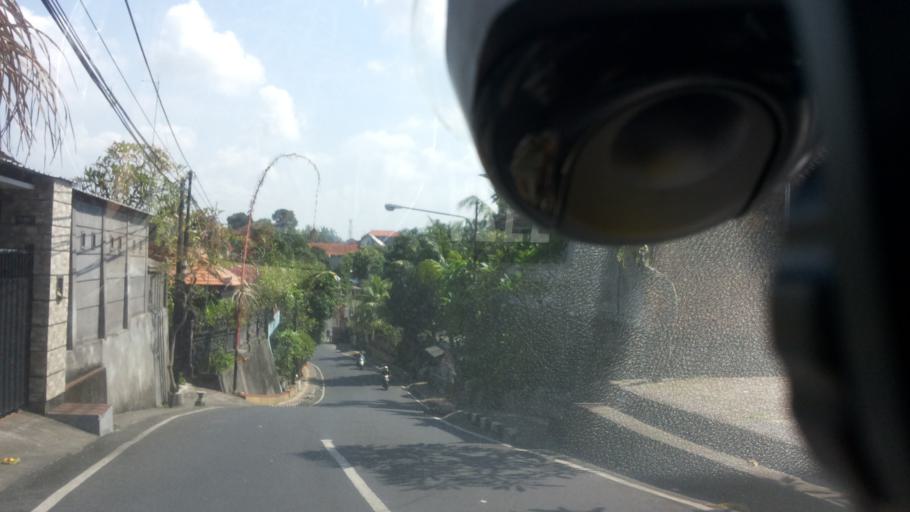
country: ID
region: Bali
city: Dajan Tangluk
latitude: -8.6401
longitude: 115.2421
